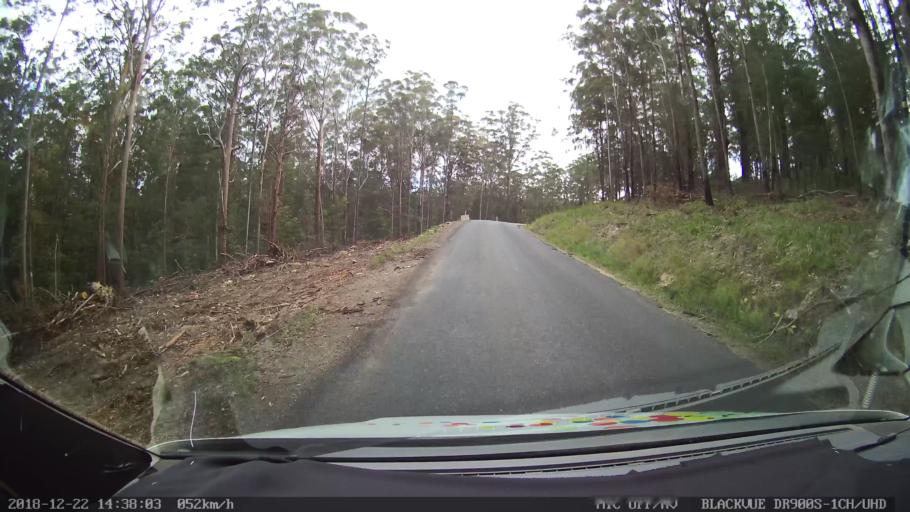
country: AU
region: New South Wales
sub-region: Bellingen
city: Dorrigo
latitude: -30.1363
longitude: 152.5997
